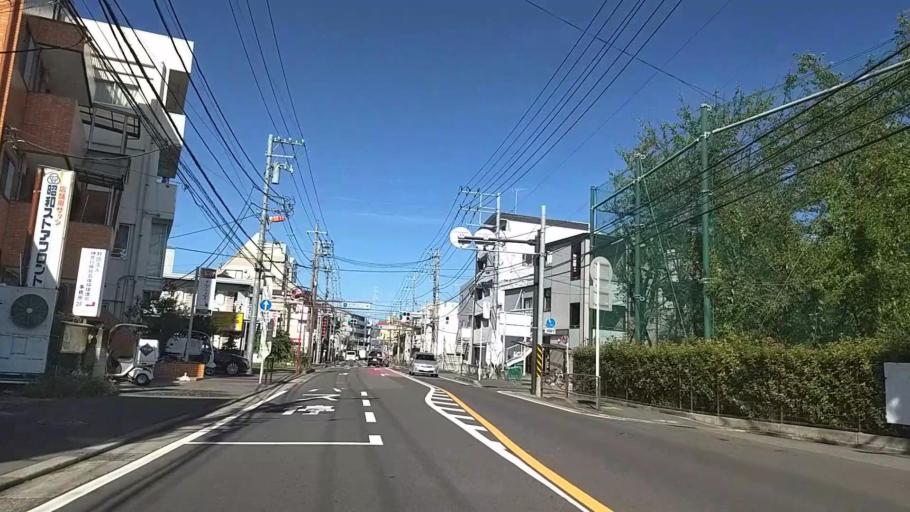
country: JP
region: Kanagawa
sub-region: Kawasaki-shi
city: Kawasaki
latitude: 35.5636
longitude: 139.6451
